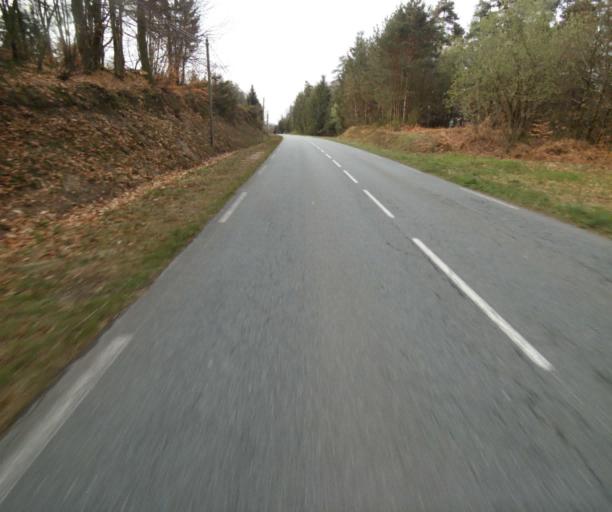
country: FR
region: Limousin
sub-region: Departement de la Correze
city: Correze
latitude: 45.3906
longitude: 1.8631
